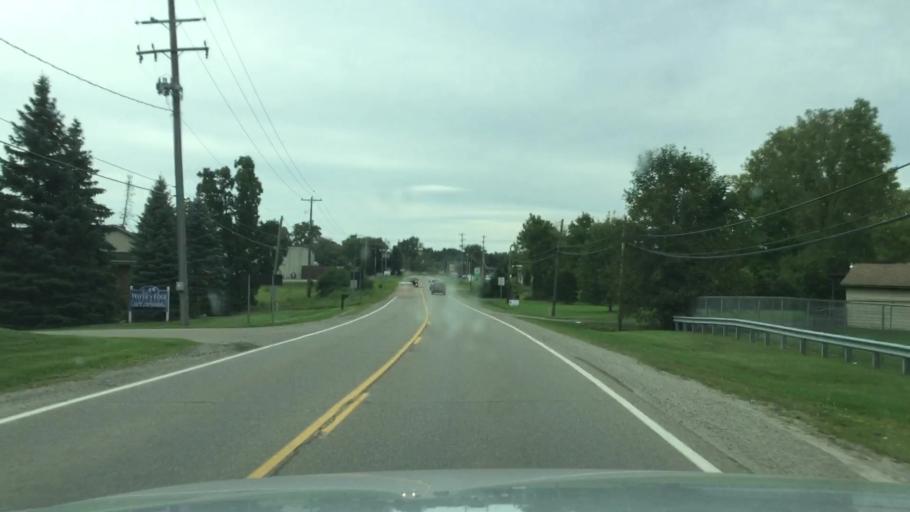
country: US
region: Michigan
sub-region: Genesee County
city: Argentine
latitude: 42.7933
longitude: -83.8404
